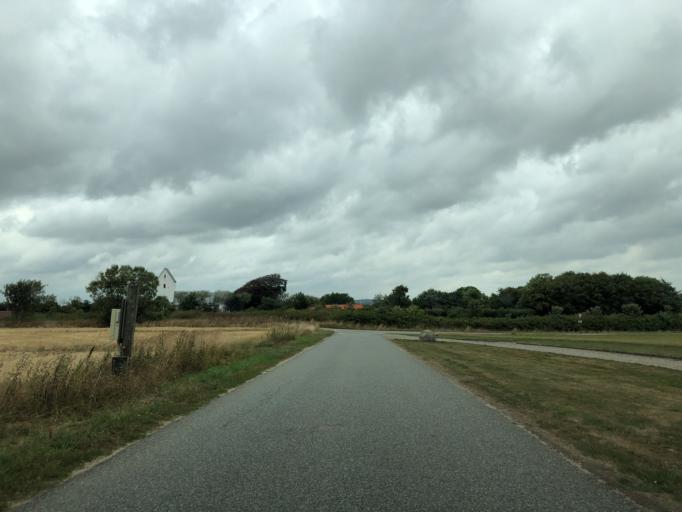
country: DK
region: Central Jutland
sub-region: Ringkobing-Skjern Kommune
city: Videbaek
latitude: 56.1103
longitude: 8.4999
